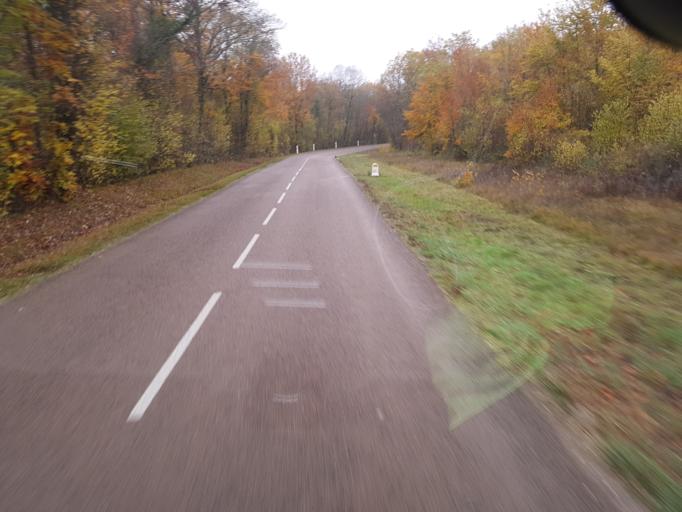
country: FR
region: Bourgogne
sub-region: Departement de la Cote-d'Or
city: Messigny-et-Vantoux
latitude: 47.5597
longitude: 4.9191
